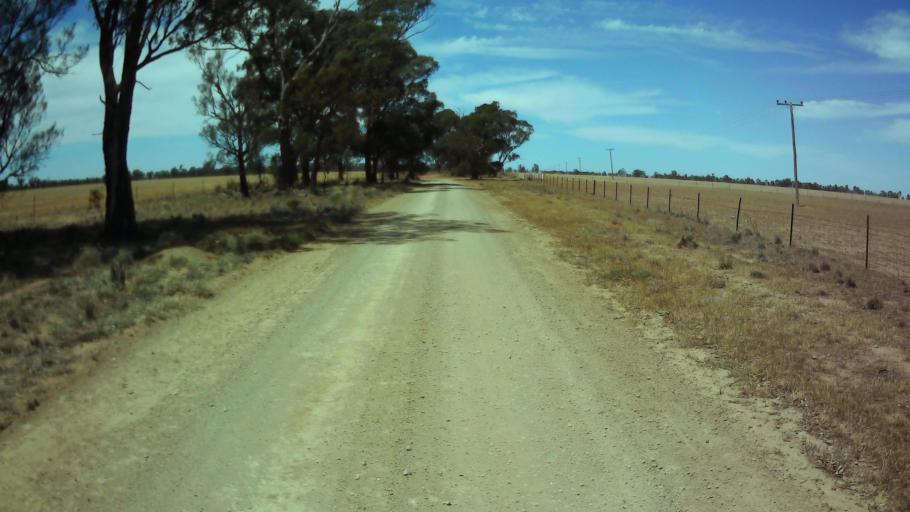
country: AU
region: New South Wales
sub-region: Weddin
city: Grenfell
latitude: -33.8898
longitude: 147.8034
